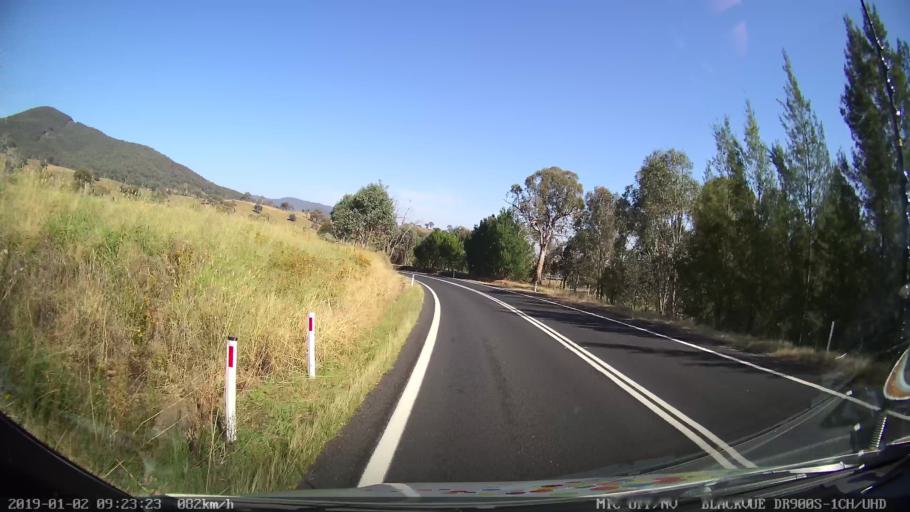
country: AU
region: New South Wales
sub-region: Tumut Shire
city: Tumut
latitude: -35.3880
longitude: 148.2971
